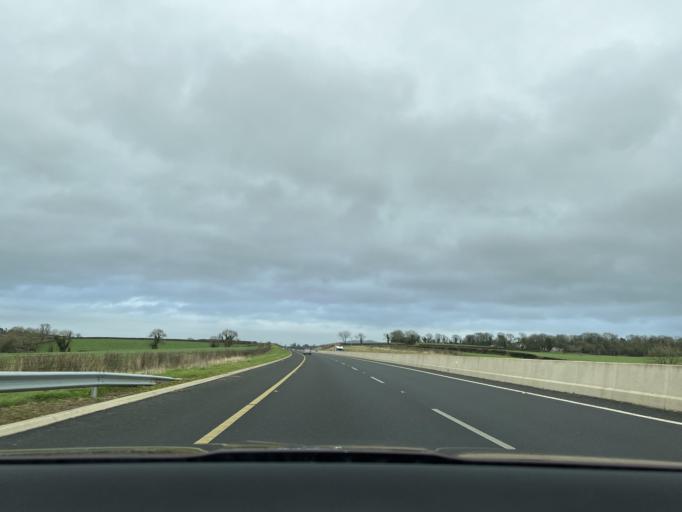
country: IE
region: Leinster
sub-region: Loch Garman
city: Ferns
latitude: 52.5532
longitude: -6.4816
